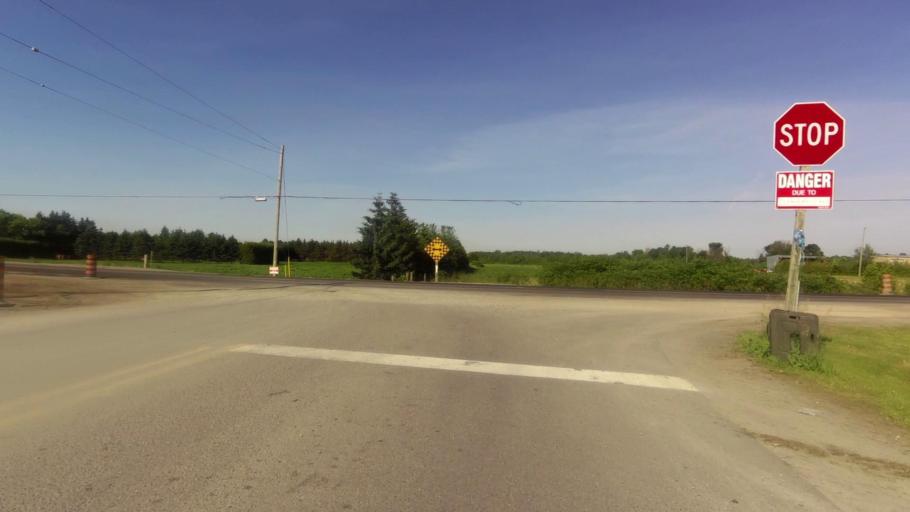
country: CA
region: Ontario
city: Ottawa
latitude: 45.2177
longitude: -75.5706
